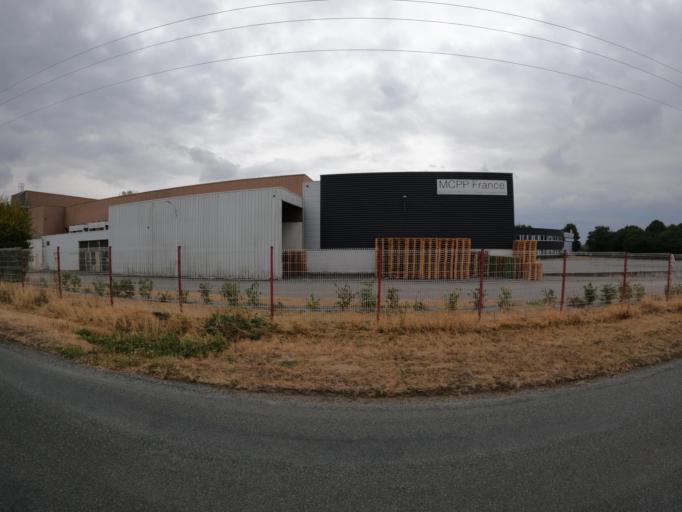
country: FR
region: Pays de la Loire
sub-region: Departement de la Vendee
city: Tiffauges
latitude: 47.0072
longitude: -1.1066
